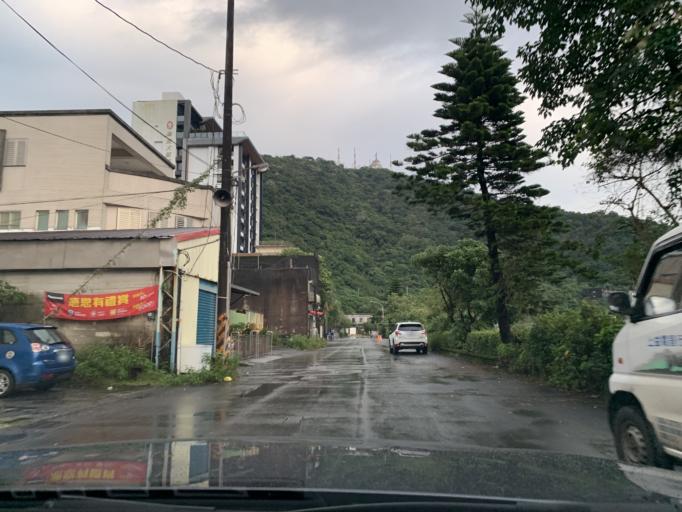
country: TW
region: Taiwan
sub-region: Yilan
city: Yilan
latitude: 24.5969
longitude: 121.8534
